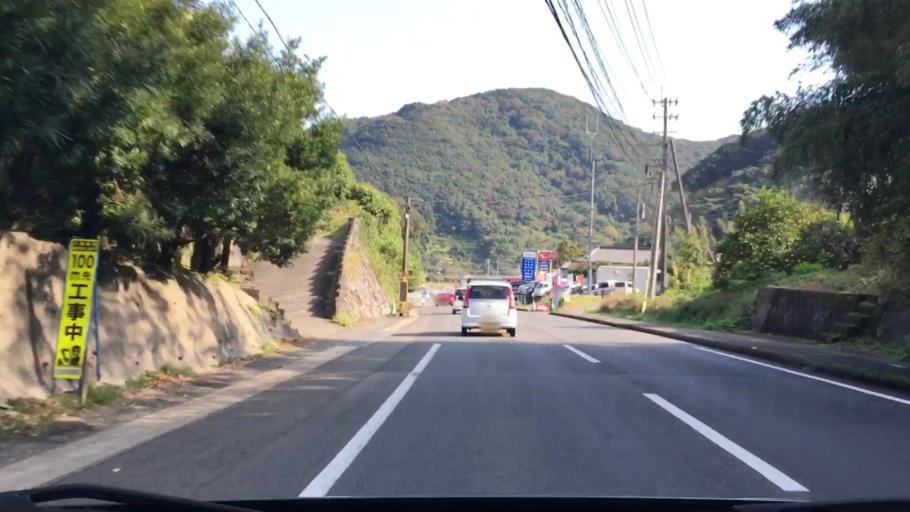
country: JP
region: Nagasaki
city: Togitsu
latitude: 32.8603
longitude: 129.8029
